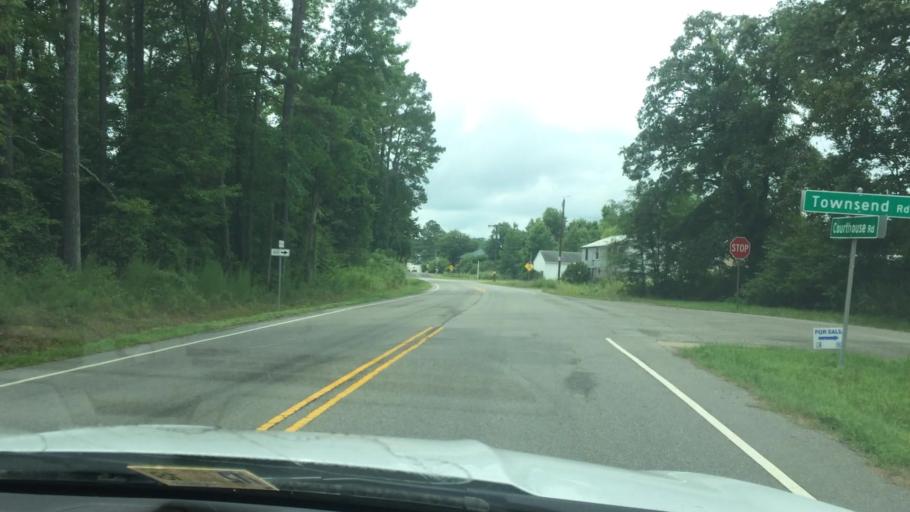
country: US
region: Virginia
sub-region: New Kent County
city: New Kent
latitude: 37.4394
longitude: -77.0394
